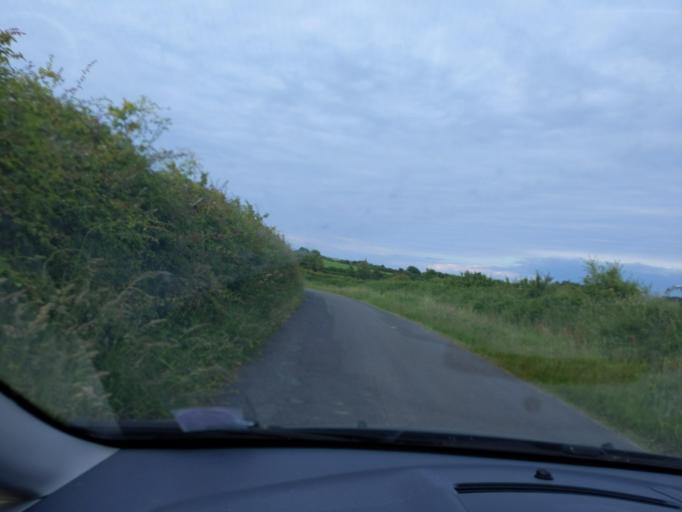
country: IM
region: Ramsey
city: Ramsey
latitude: 54.3633
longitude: -4.4395
